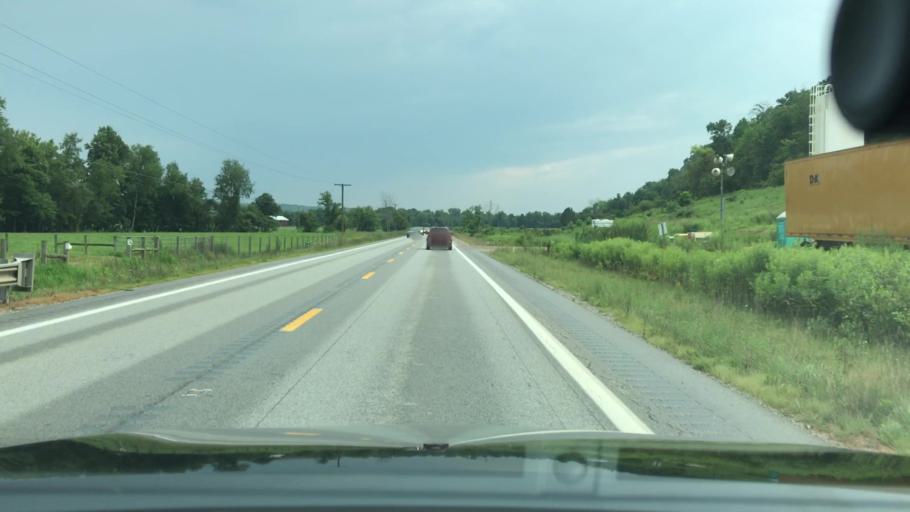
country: US
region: West Virginia
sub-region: Putnam County
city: Buffalo
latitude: 38.6351
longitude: -81.9776
